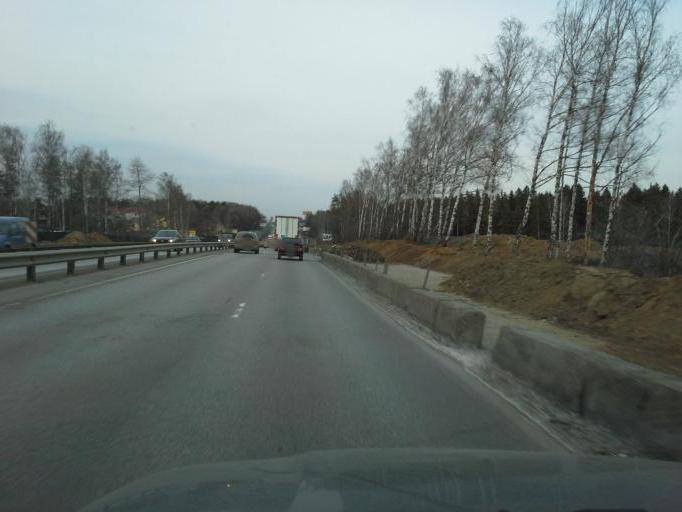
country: RU
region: Moskovskaya
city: Odintsovo
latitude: 55.6631
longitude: 37.3043
